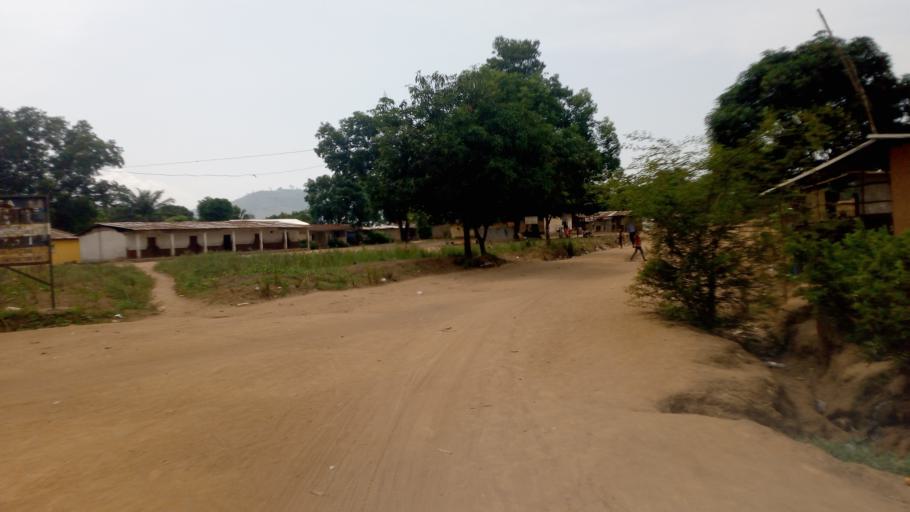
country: SL
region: Western Area
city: Waterloo
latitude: 8.3137
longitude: -13.0652
